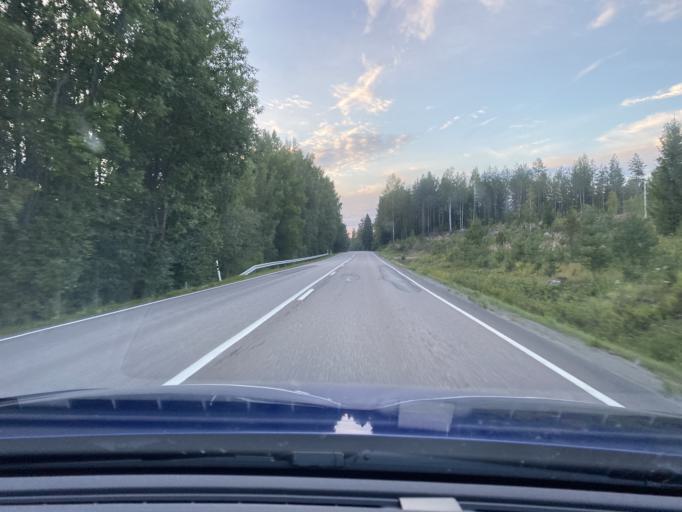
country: FI
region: Satakunta
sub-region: Pohjois-Satakunta
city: Honkajoki
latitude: 61.9346
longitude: 22.2399
